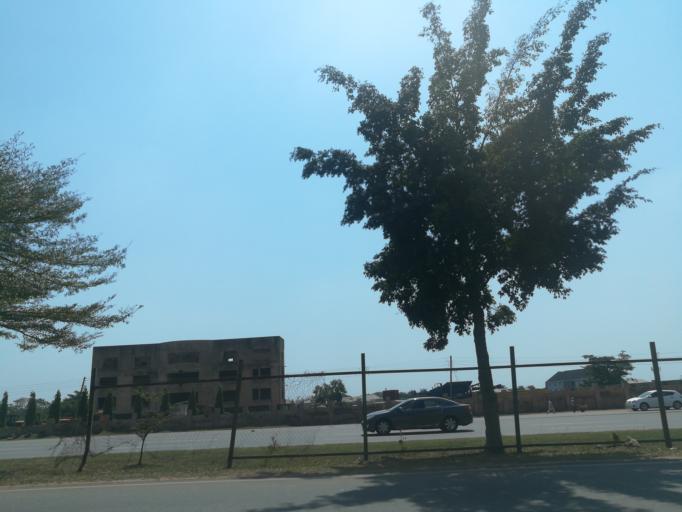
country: NG
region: Abuja Federal Capital Territory
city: Abuja
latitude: 9.0775
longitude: 7.4468
